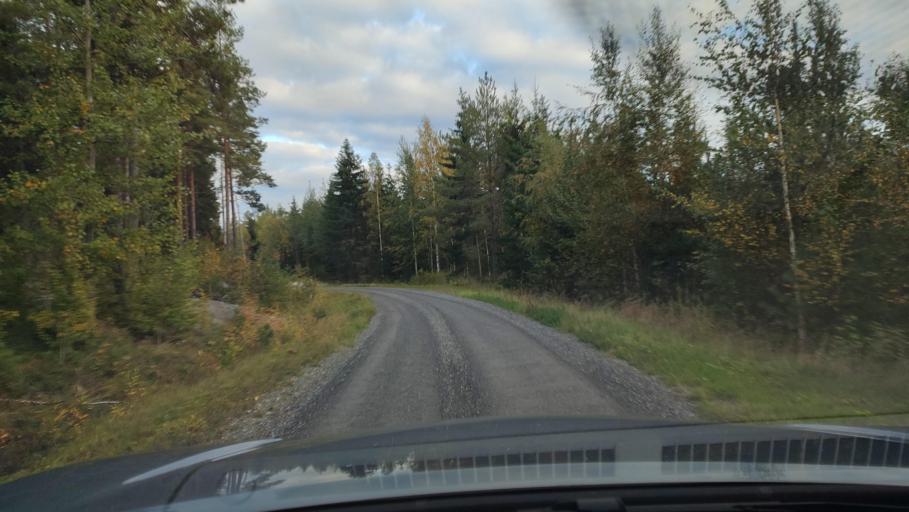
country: FI
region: Ostrobothnia
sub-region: Sydosterbotten
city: Kristinestad
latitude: 62.2322
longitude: 21.4120
